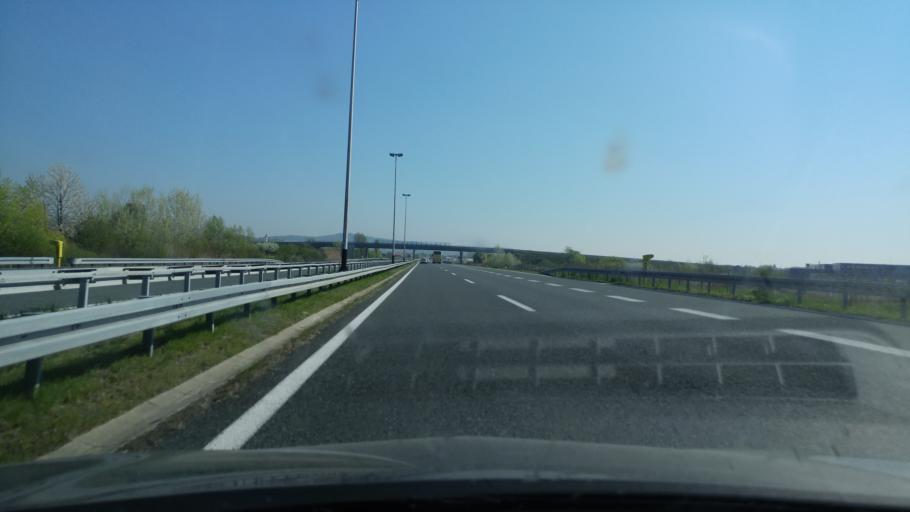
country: HR
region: Brodsko-Posavska
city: Podvinje
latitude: 45.1814
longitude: 18.0087
